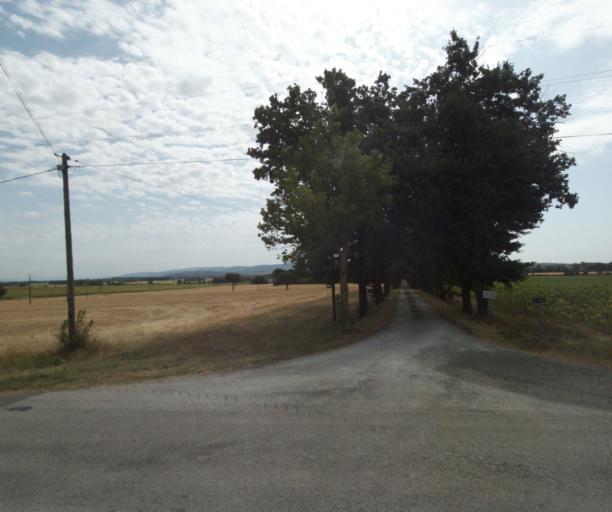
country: FR
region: Midi-Pyrenees
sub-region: Departement de la Haute-Garonne
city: Saint-Felix-Lauragais
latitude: 43.4342
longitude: 1.9037
